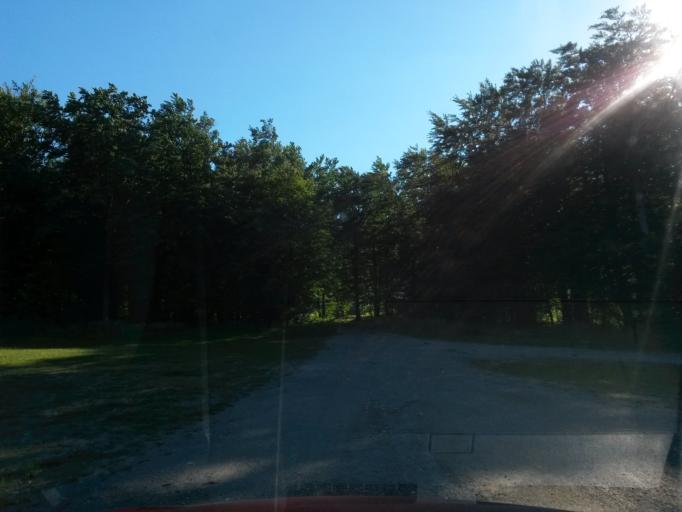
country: SK
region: Kosicky
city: Kosice
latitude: 48.7672
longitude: 21.1340
